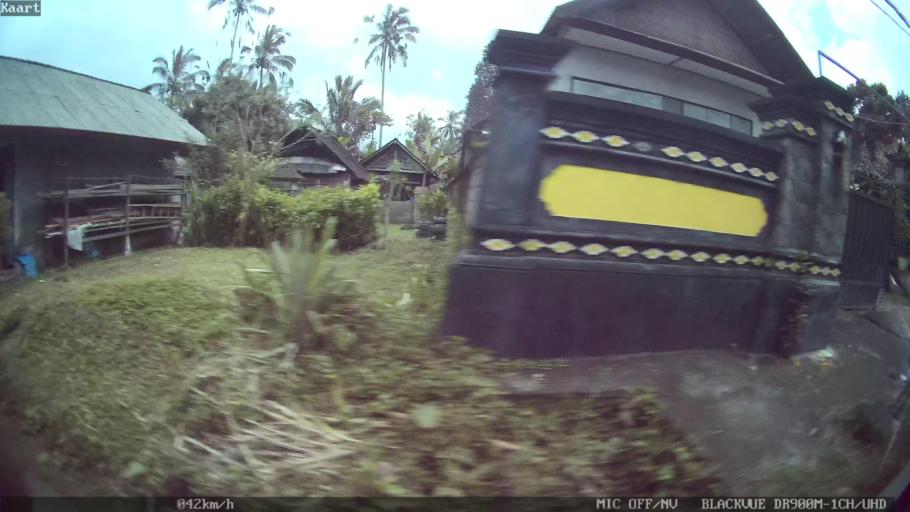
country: ID
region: Bali
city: Banjar Geriana Kangin
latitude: -8.4109
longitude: 115.4385
